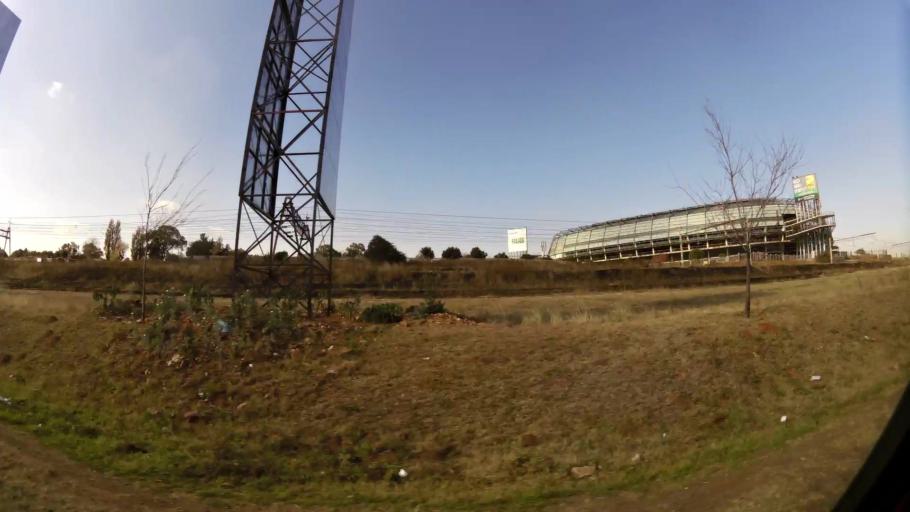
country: ZA
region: Gauteng
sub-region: City of Johannesburg Metropolitan Municipality
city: Soweto
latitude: -26.2297
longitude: 27.9225
